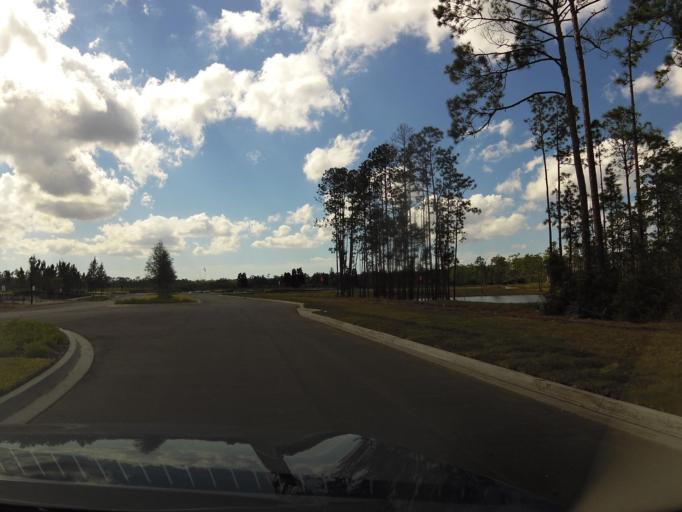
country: US
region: Florida
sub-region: Saint Johns County
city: Ponte Vedra Beach
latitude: 30.2473
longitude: -81.4973
